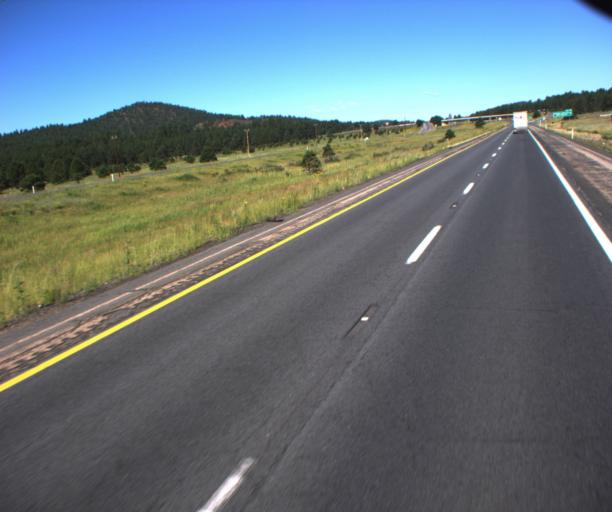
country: US
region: Arizona
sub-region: Coconino County
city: Parks
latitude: 35.2630
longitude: -112.0415
